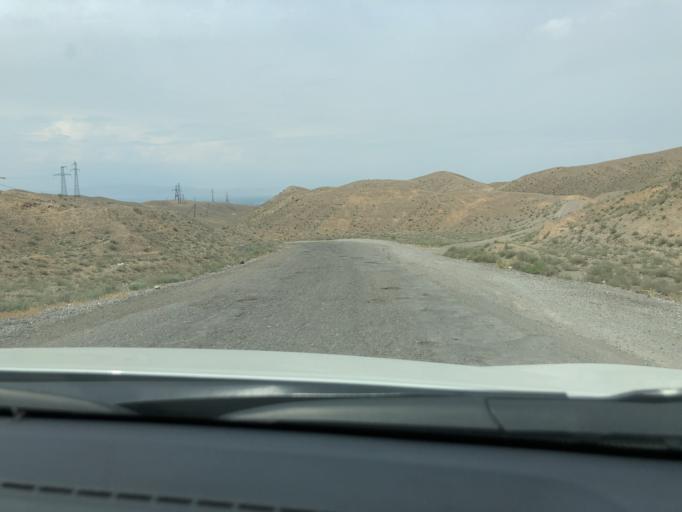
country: TJ
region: Viloyati Sughd
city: Kim
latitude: 40.2180
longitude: 70.4799
